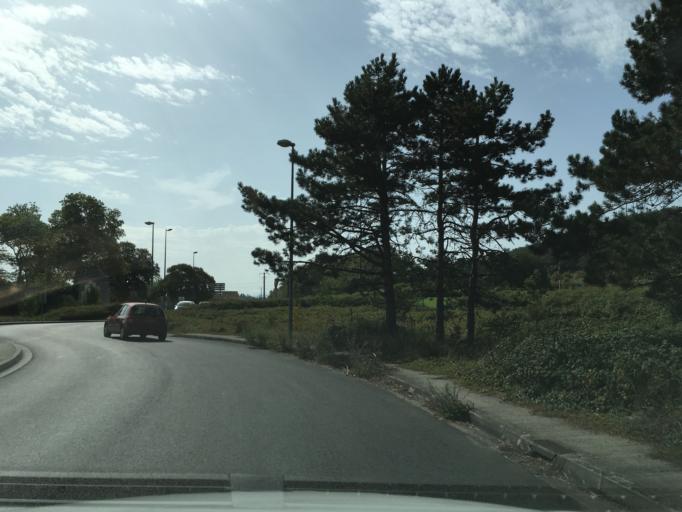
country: FR
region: Midi-Pyrenees
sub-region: Departement du Tarn
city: Lagarrigue
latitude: 43.5886
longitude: 2.2707
